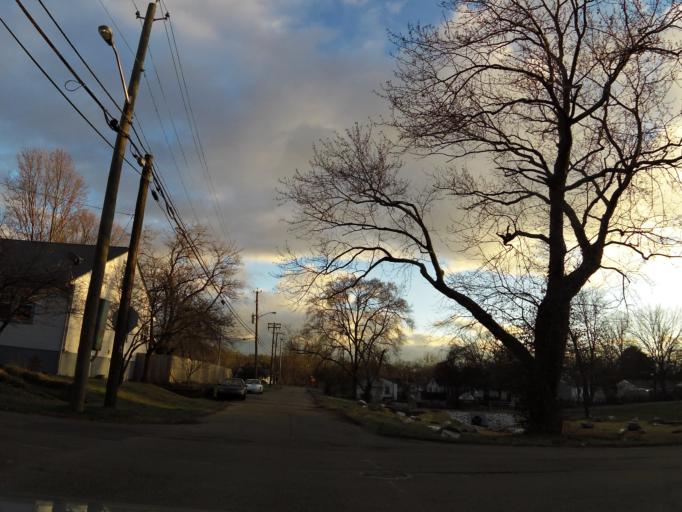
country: US
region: Tennessee
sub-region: Knox County
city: Knoxville
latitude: 35.9961
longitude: -83.9346
